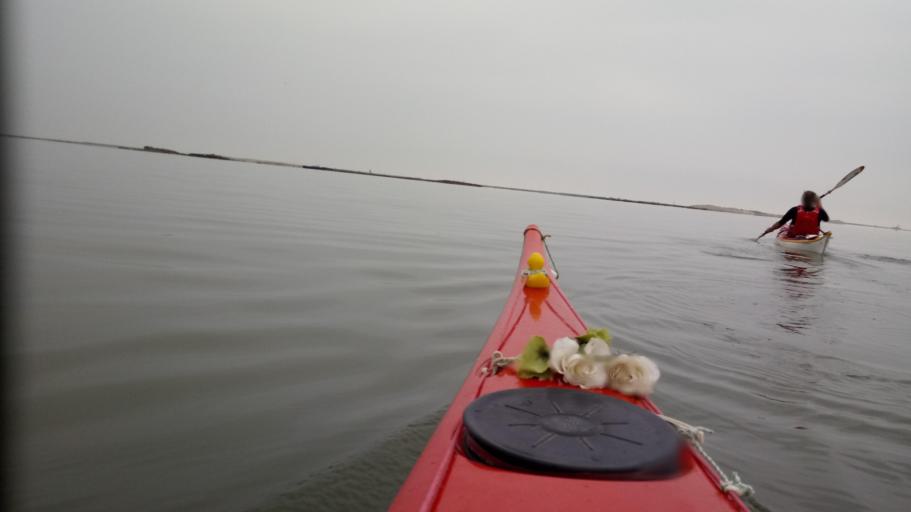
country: NL
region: Flevoland
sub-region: Gemeente Lelystad
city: Lelystad
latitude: 52.6059
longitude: 5.3840
